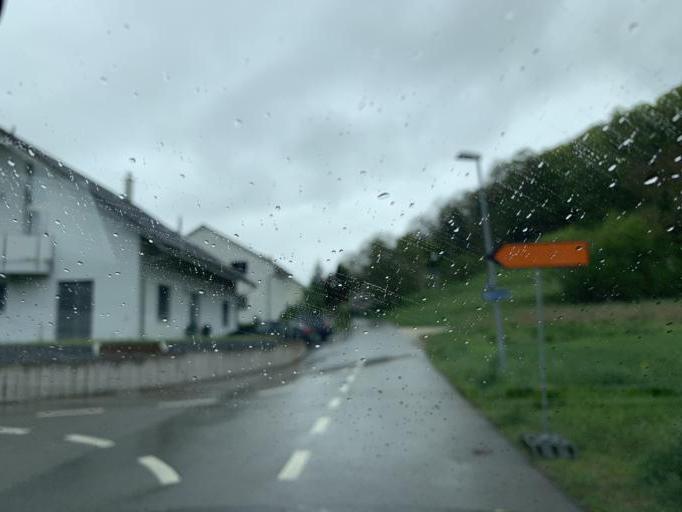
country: CH
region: Schaffhausen
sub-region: Bezirk Schaffhausen
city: Beringen
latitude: 47.7015
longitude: 8.5708
